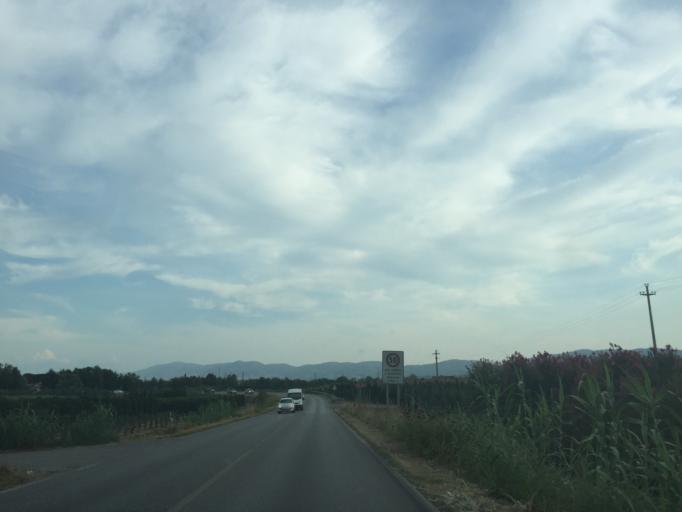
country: IT
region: Tuscany
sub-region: Provincia di Pistoia
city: Pistoia
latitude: 43.9592
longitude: 10.8956
